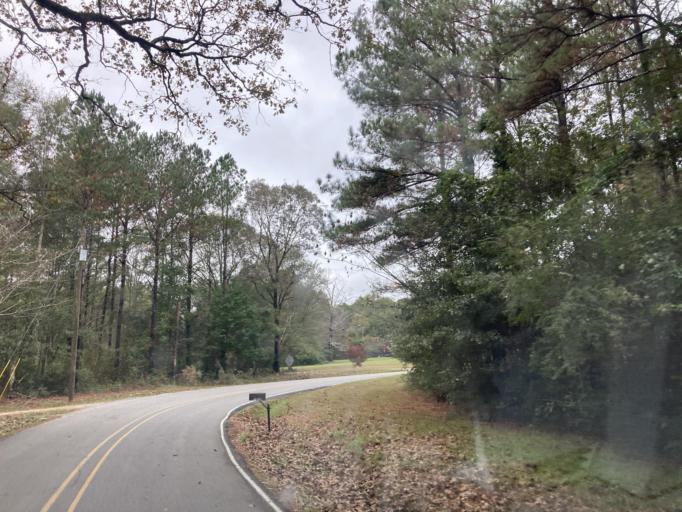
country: US
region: Mississippi
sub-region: Lamar County
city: Purvis
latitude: 31.1764
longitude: -89.4186
